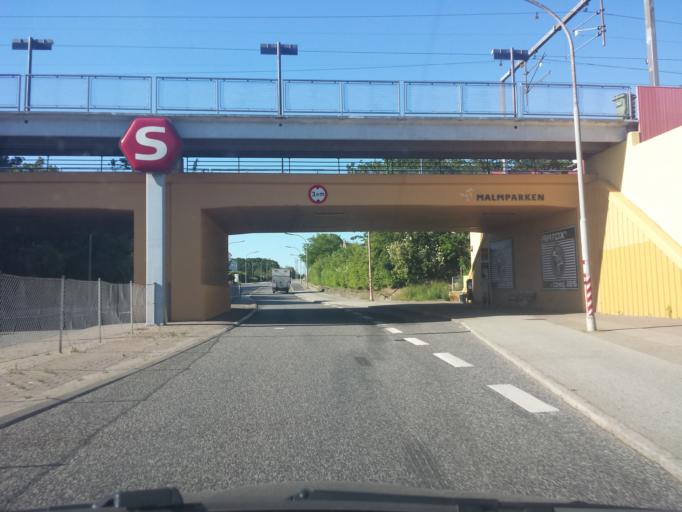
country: DK
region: Capital Region
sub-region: Ballerup Kommune
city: Ballerup
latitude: 55.7244
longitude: 12.3857
